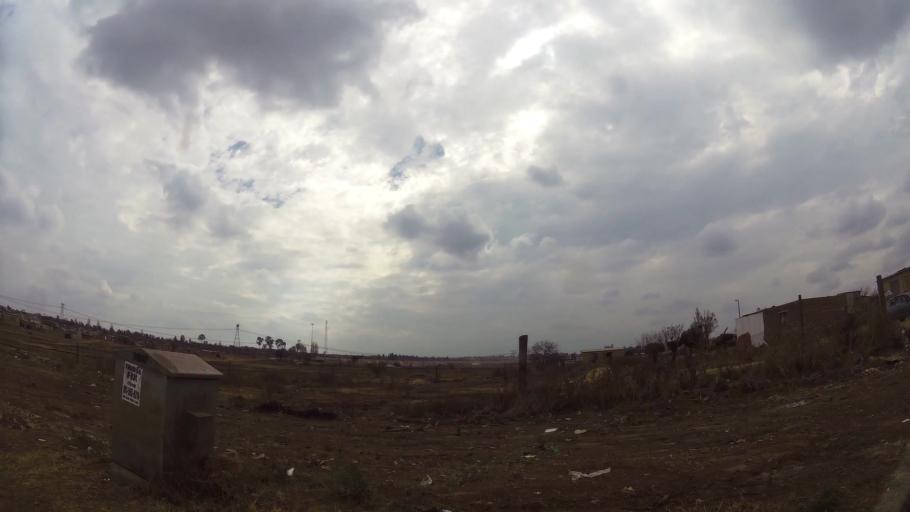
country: ZA
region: Gauteng
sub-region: Ekurhuleni Metropolitan Municipality
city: Germiston
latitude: -26.3798
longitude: 28.1161
